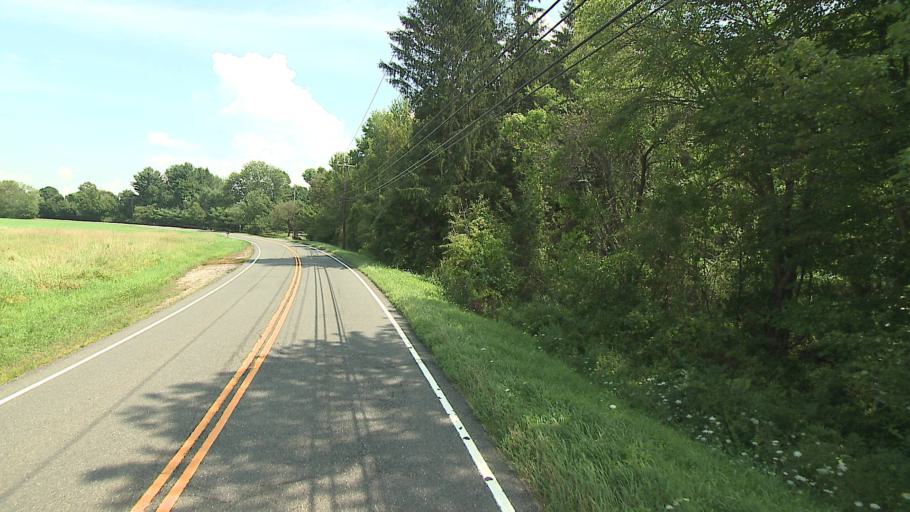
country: US
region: Connecticut
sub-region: Litchfield County
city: New Preston
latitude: 41.6346
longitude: -73.3396
